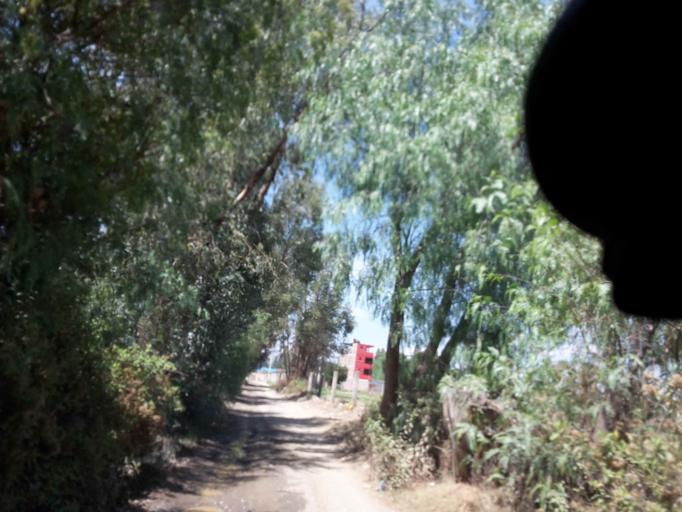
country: BO
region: Cochabamba
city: Cochabamba
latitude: -17.3616
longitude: -66.2225
